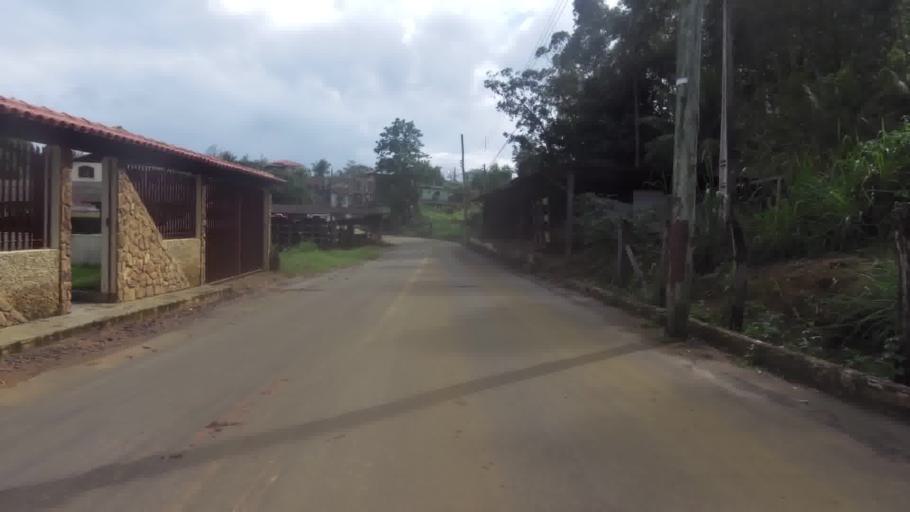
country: BR
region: Espirito Santo
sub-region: Piuma
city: Piuma
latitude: -20.8244
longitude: -40.6955
